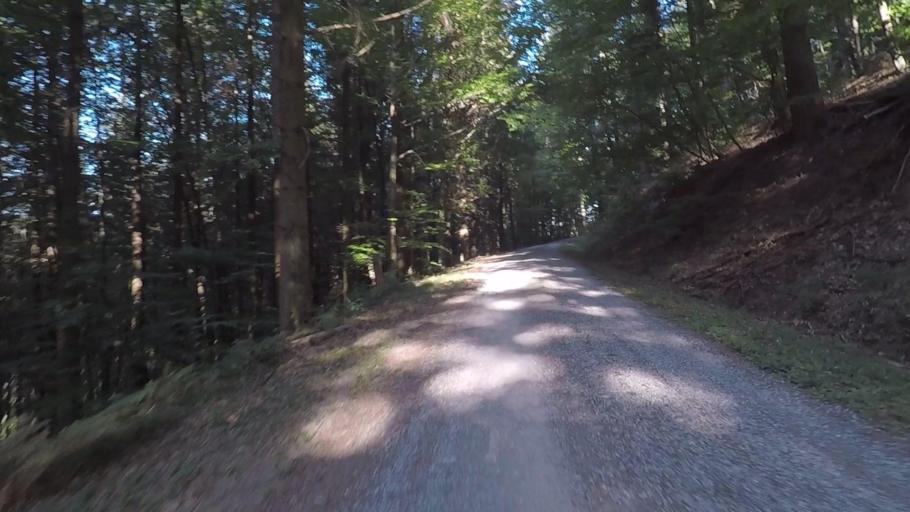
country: DE
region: Baden-Wuerttemberg
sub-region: Regierungsbezirk Stuttgart
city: Spiegelberg
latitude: 49.0449
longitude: 9.4508
